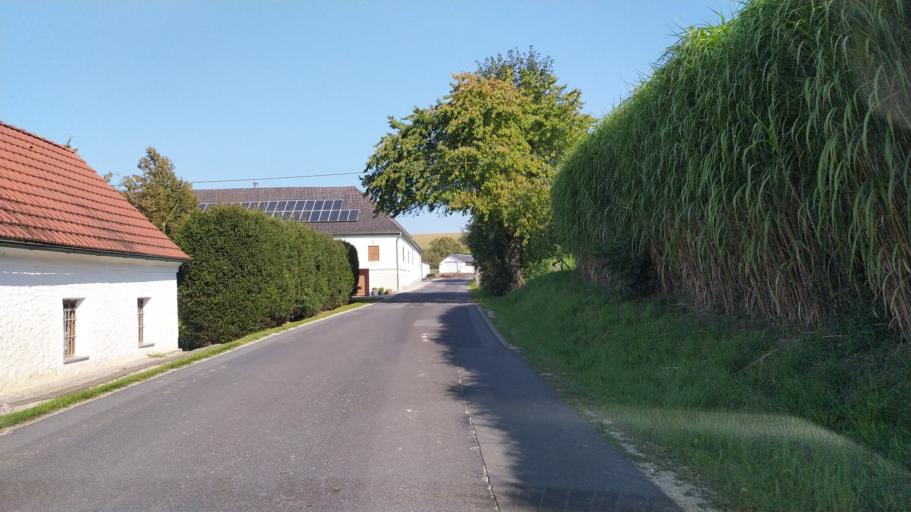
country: AT
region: Lower Austria
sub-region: Politischer Bezirk Amstetten
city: Zeillern
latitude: 48.1091
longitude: 14.7501
